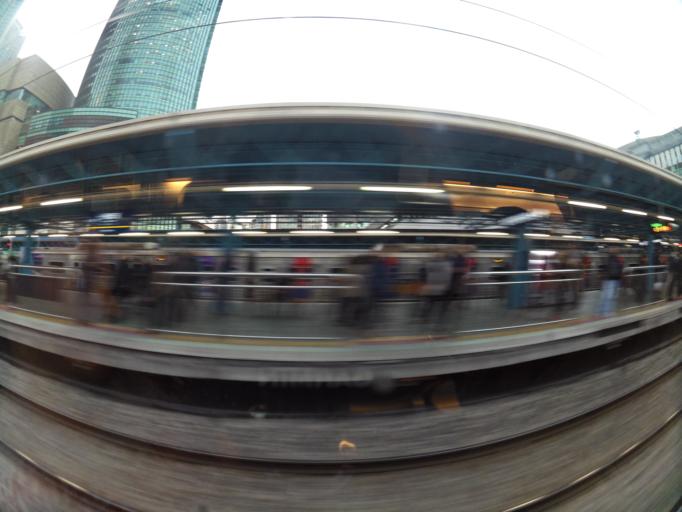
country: KR
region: Gyeonggi-do
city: Kwangmyong
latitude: 37.5086
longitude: 126.8907
